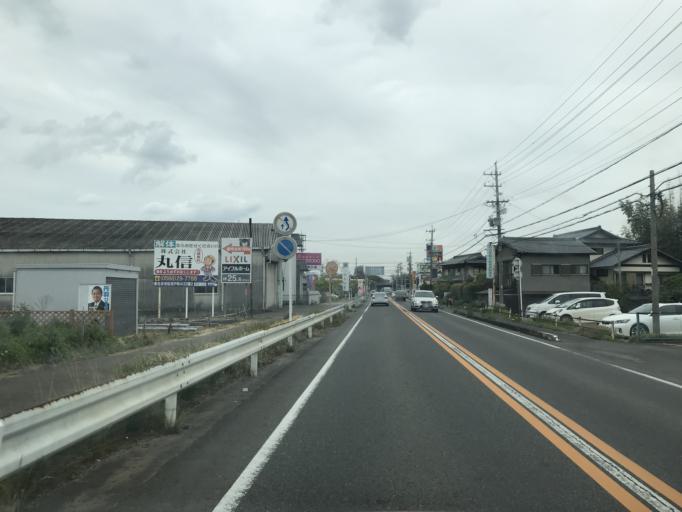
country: JP
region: Aichi
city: Kasugai
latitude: 35.2760
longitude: 136.9741
